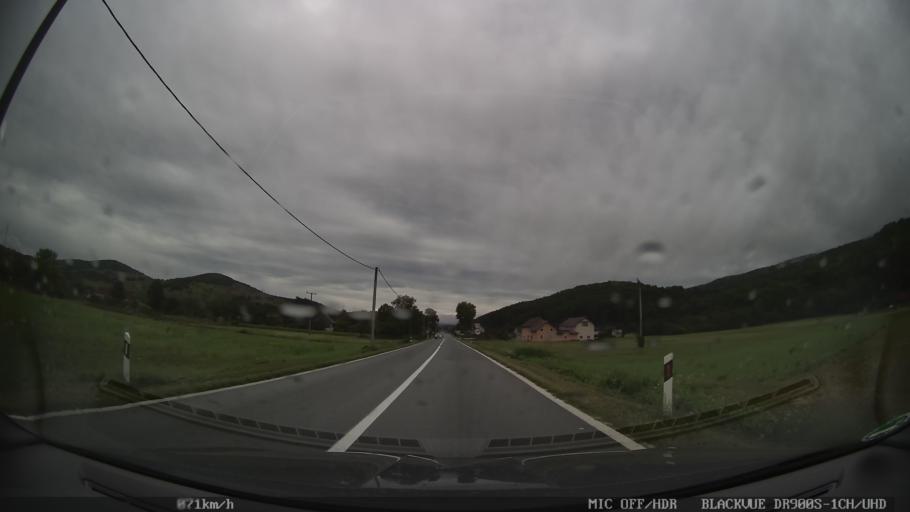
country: HR
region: Licko-Senjska
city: Brinje
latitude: 44.9375
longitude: 15.1273
